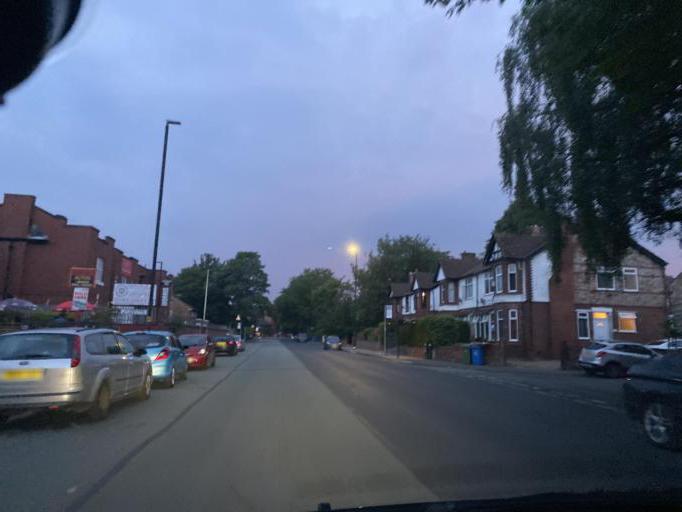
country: GB
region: England
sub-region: Manchester
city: Chorlton cum Hardy
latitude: 53.4519
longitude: -2.2696
